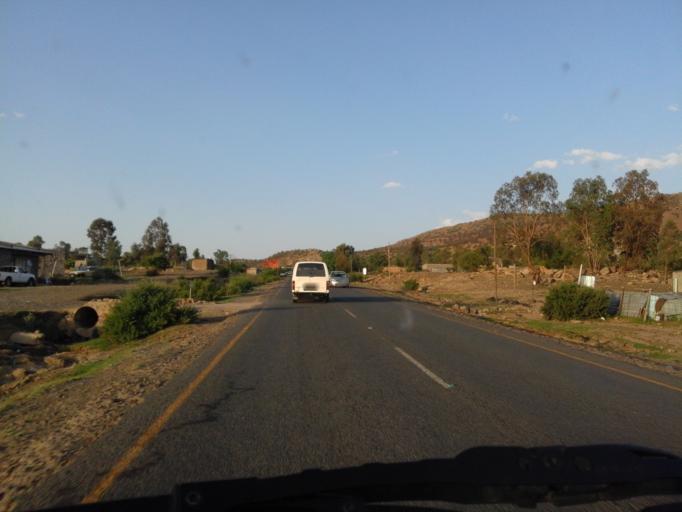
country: LS
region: Mafeteng
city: Mafeteng
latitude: -29.8422
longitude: 27.2310
